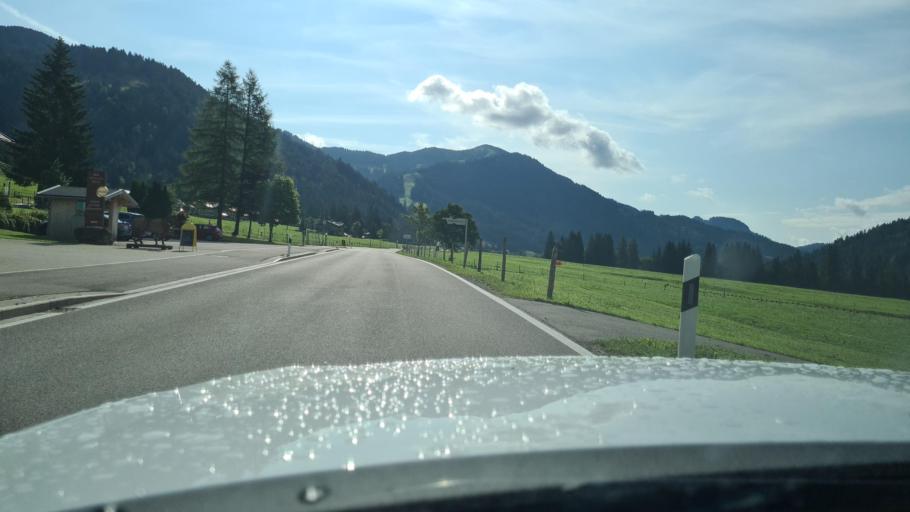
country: DE
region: Bavaria
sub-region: Swabia
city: Balderschwang
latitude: 47.4654
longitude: 10.1092
